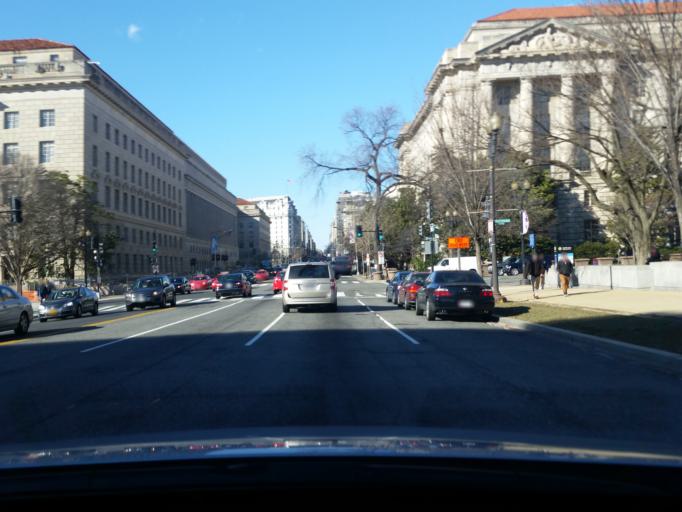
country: US
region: Washington, D.C.
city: Washington, D.C.
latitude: 38.8916
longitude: -77.0319
